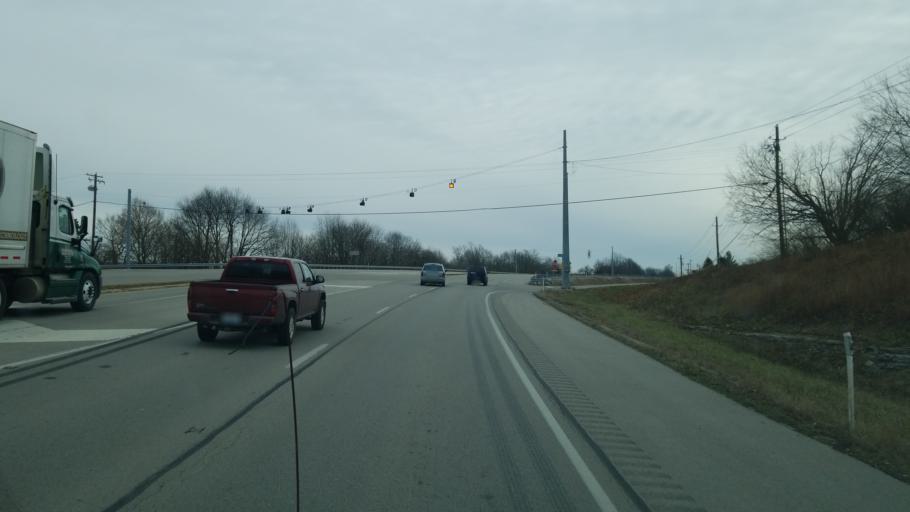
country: US
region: Kentucky
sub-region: Bourbon County
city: Paris
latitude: 38.2269
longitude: -84.2478
